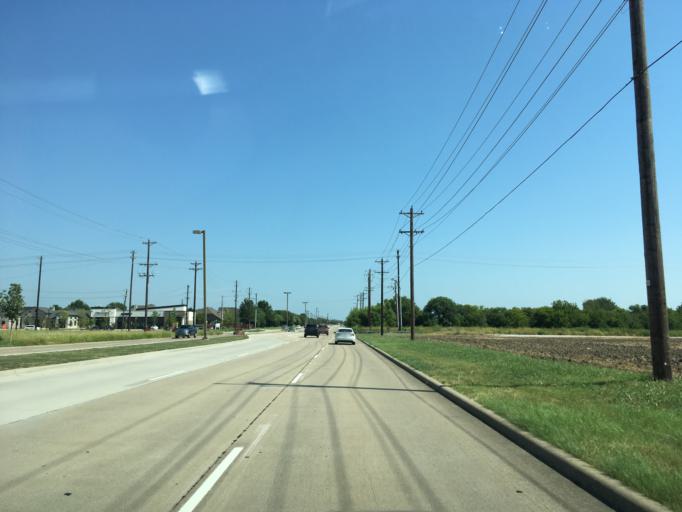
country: US
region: Texas
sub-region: Collin County
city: Allen
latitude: 33.1488
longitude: -96.6806
